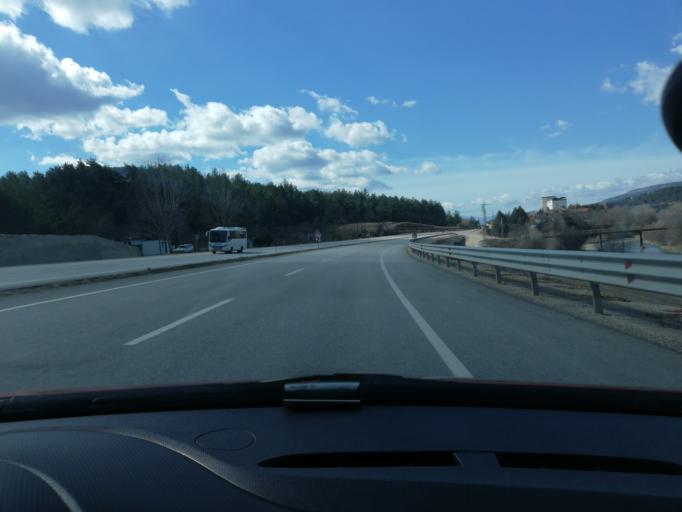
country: TR
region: Karabuk
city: Ovacik
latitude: 41.2003
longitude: 32.9368
